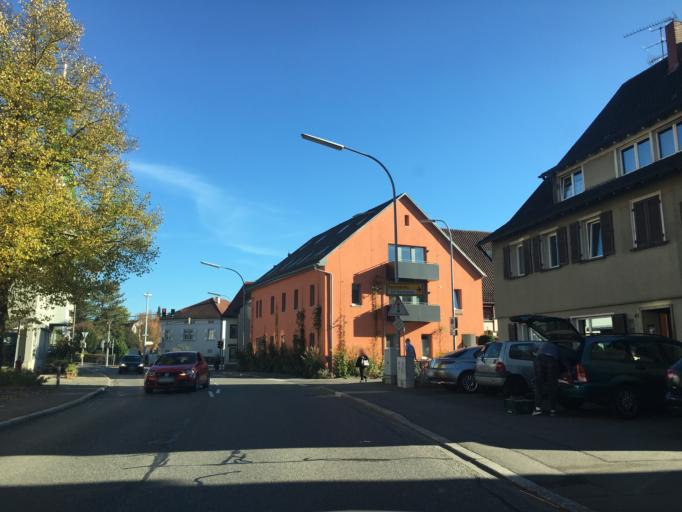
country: CH
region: Thurgau
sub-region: Kreuzlingen District
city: Gottlieben
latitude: 47.6930
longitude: 9.1450
